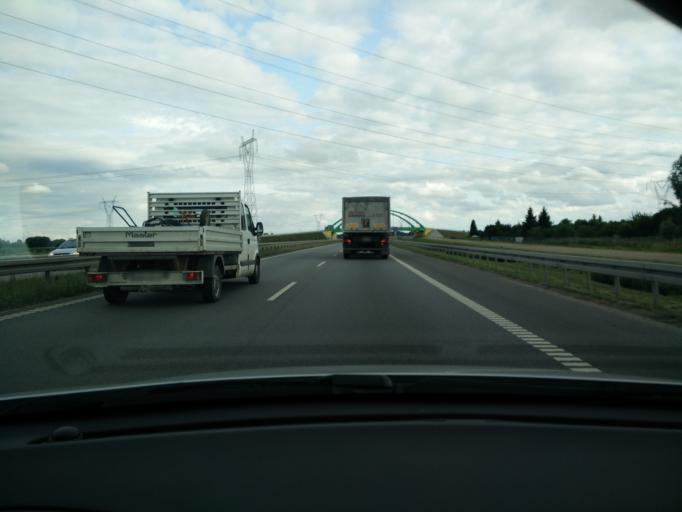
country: PL
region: Pomeranian Voivodeship
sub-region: Gdansk
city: Gdansk
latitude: 54.3358
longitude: 18.7023
